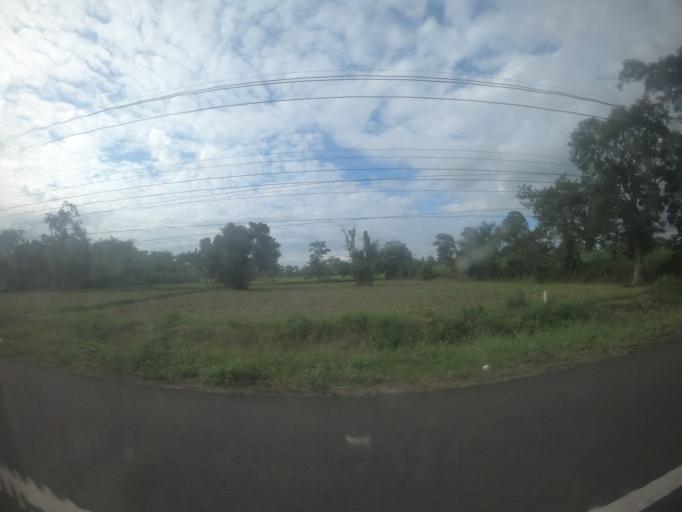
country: TH
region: Surin
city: Prasat
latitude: 14.5917
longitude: 103.4500
